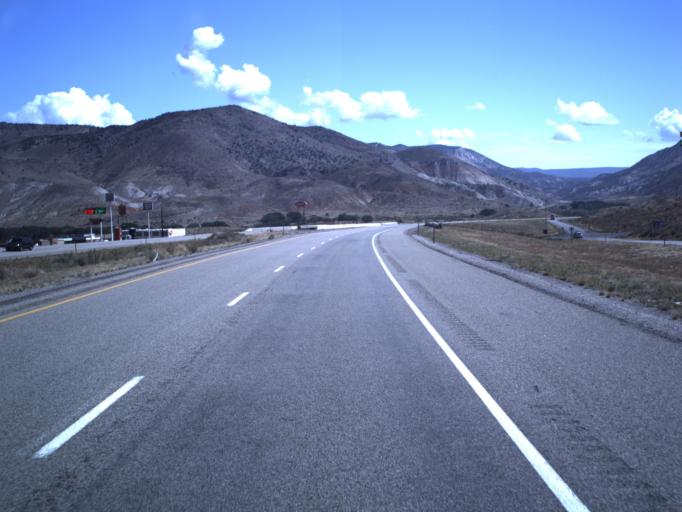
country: US
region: Utah
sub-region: Sevier County
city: Salina
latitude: 38.9334
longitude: -111.8575
